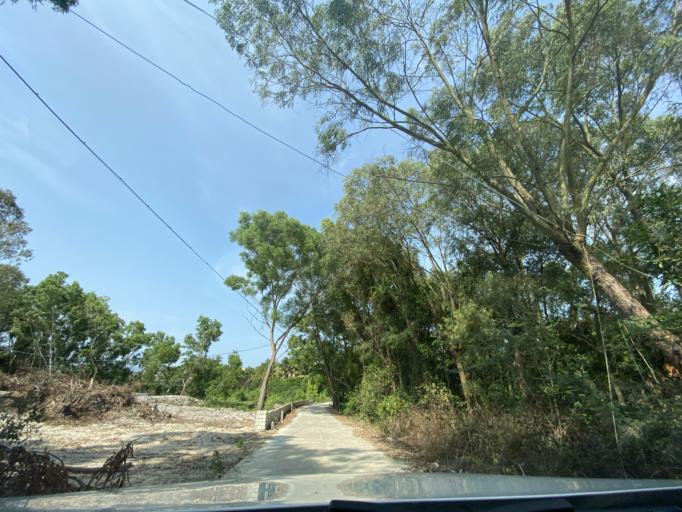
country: CN
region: Hainan
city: Yingzhou
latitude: 18.4094
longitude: 109.8320
